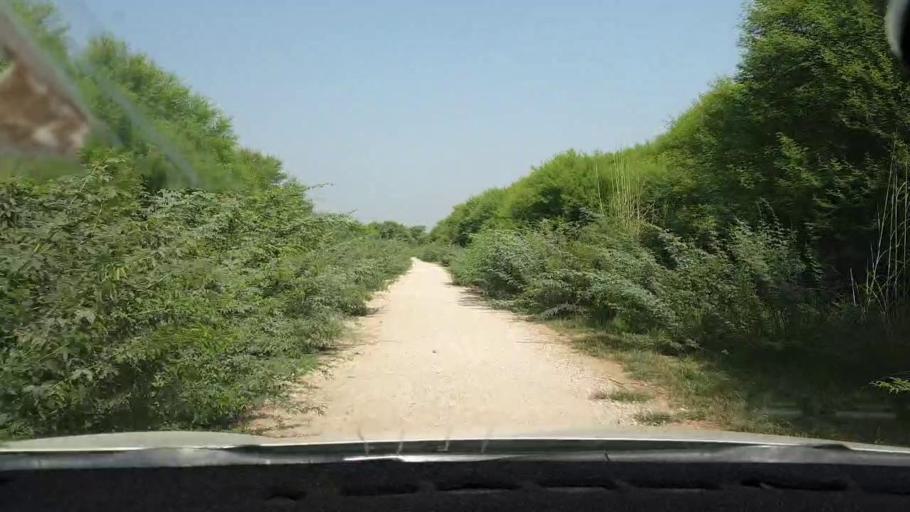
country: PK
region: Sindh
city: Tando Mittha Khan
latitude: 25.9459
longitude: 69.2982
